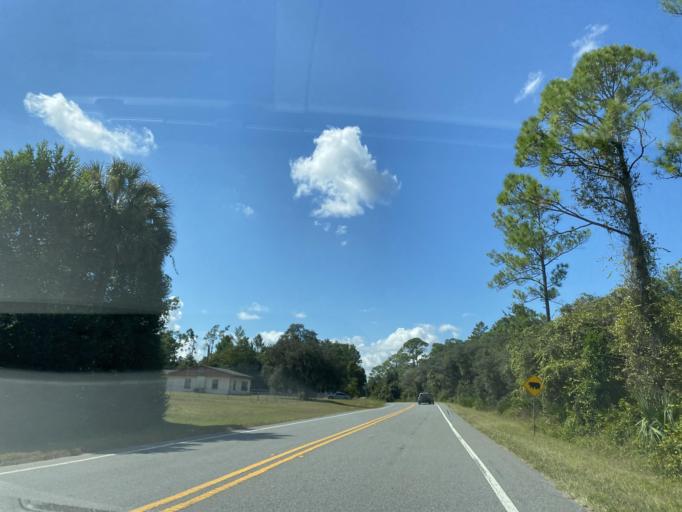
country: US
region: Florida
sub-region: Lake County
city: Lake Mack-Forest Hills
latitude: 29.0175
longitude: -81.4837
